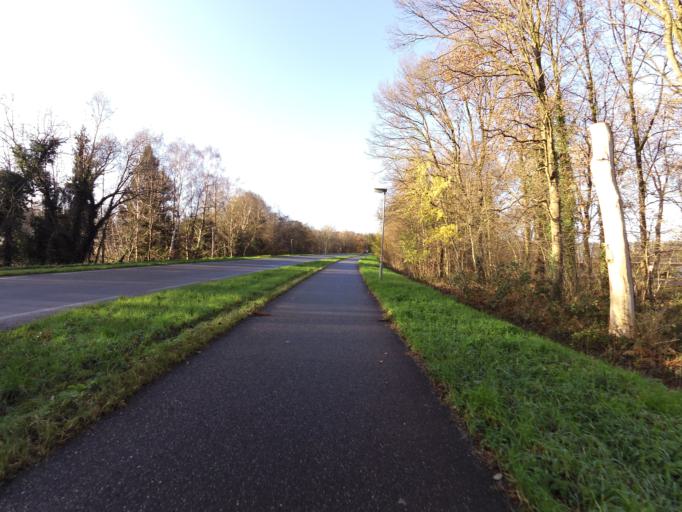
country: NL
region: Gelderland
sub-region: Gemeente Doesburg
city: Doesburg
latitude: 51.9309
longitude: 6.1716
